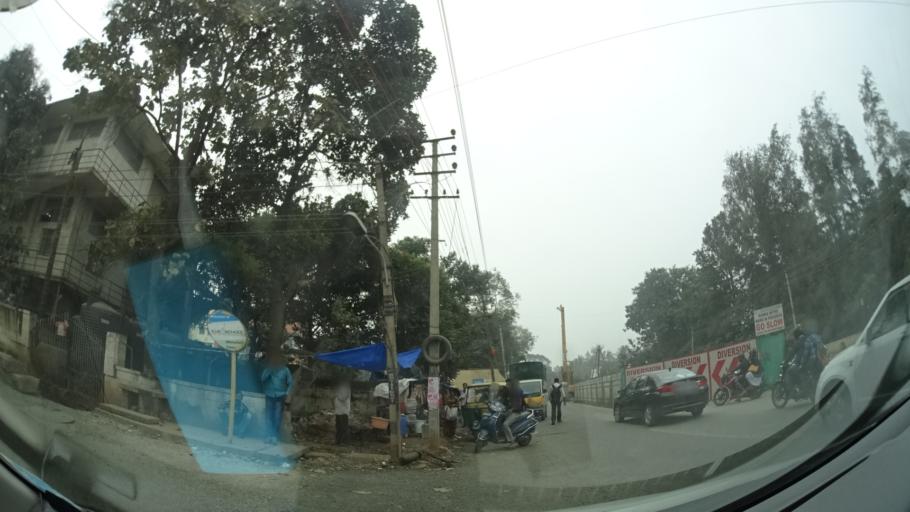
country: IN
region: Karnataka
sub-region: Bangalore Urban
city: Bangalore
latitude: 12.9843
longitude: 77.7083
